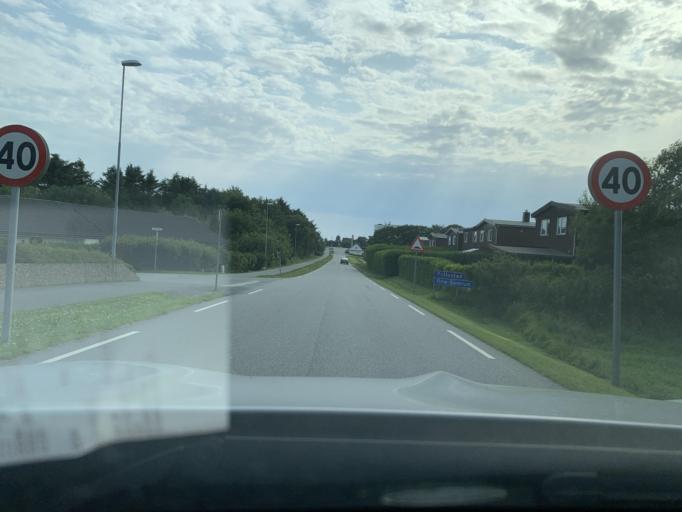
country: NO
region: Rogaland
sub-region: Time
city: Bryne
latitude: 58.7207
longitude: 5.5730
